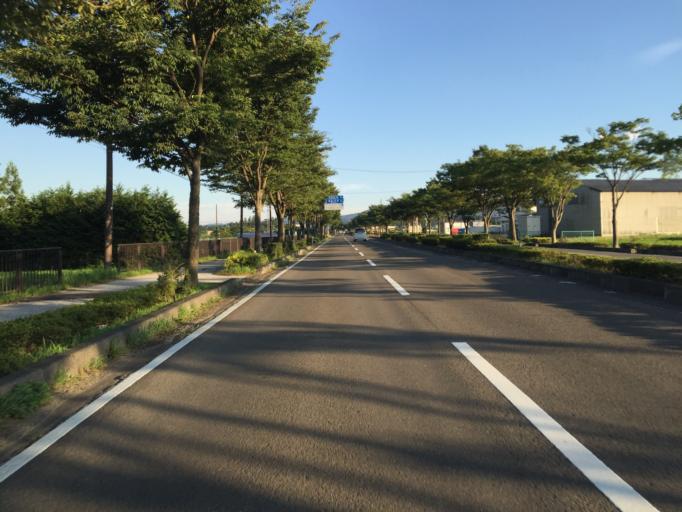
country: JP
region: Fukushima
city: Fukushima-shi
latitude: 37.7474
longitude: 140.3811
